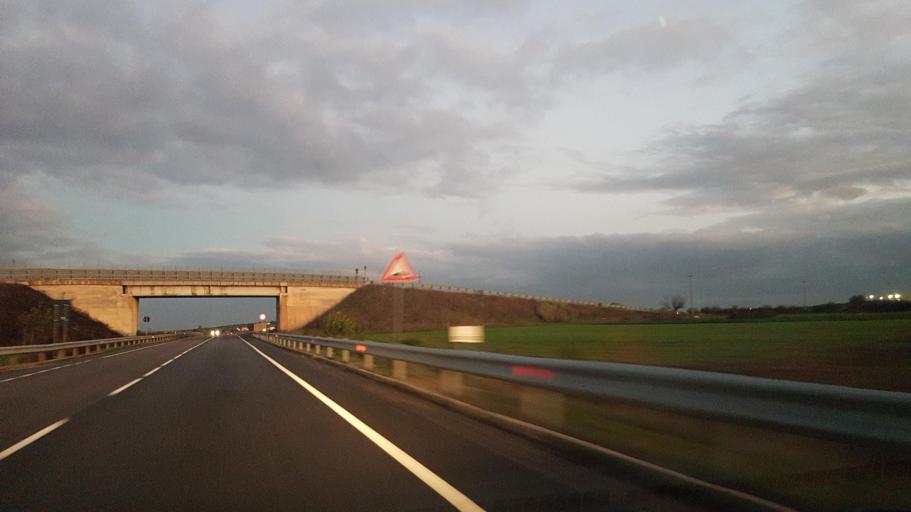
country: IT
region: Apulia
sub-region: Provincia di Taranto
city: Laterza
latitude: 40.6539
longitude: 16.7948
